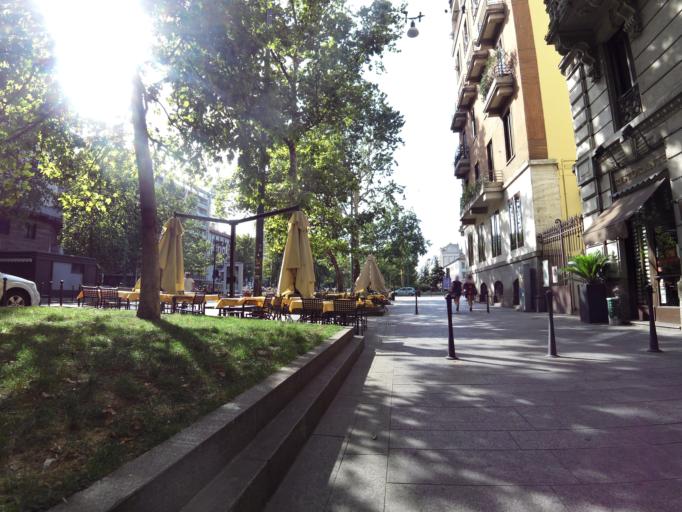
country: IT
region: Lombardy
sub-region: Citta metropolitana di Milano
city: Milano
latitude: 45.4776
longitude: 9.1699
